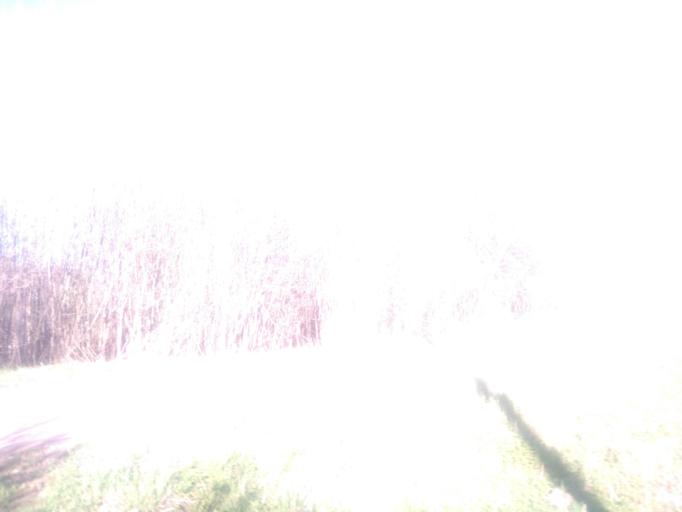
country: LV
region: Vecpiebalga
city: Vecpiebalga
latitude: 57.0232
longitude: 25.8534
